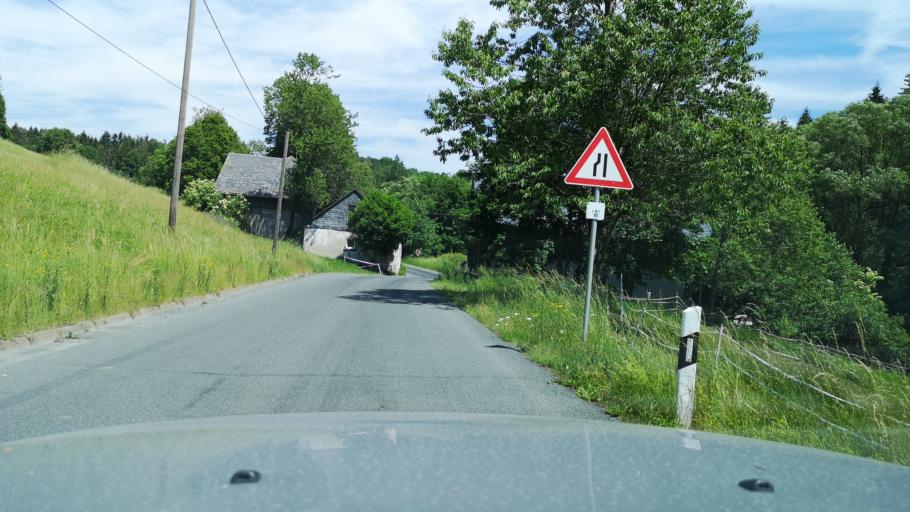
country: DE
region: Bavaria
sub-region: Upper Franconia
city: Geroldsgrun
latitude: 50.3652
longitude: 11.5835
